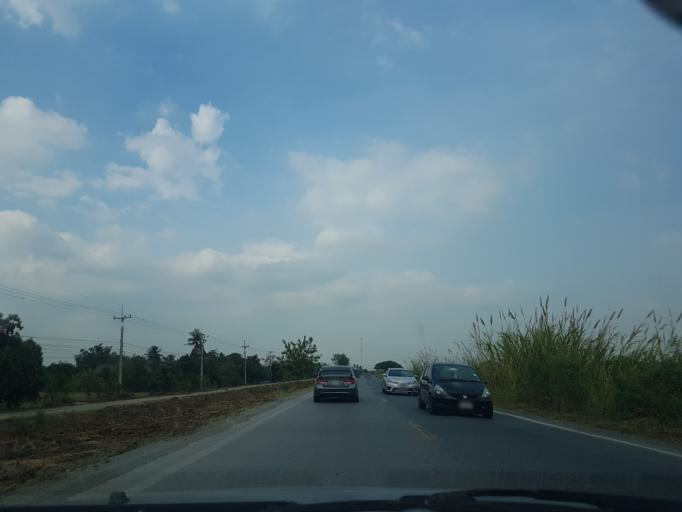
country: TH
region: Sara Buri
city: Nong Saeng
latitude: 14.5006
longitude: 100.7349
